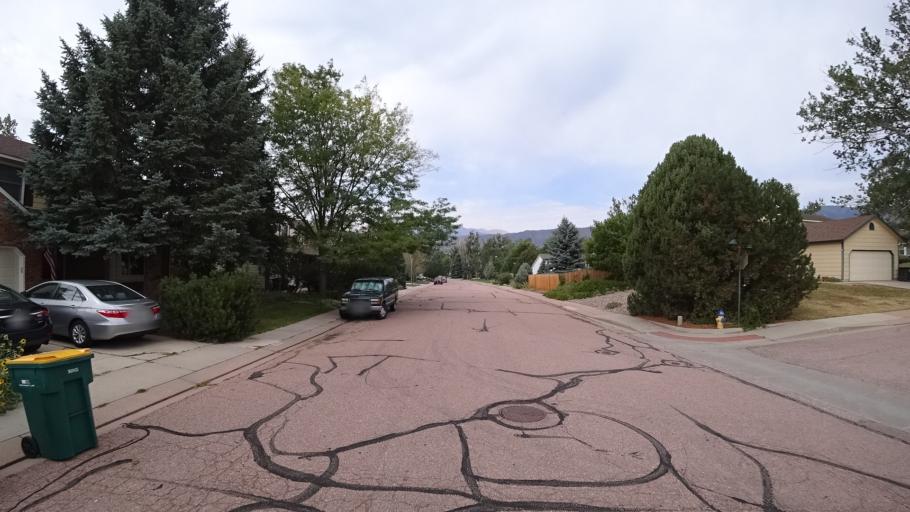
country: US
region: Colorado
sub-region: El Paso County
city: Air Force Academy
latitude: 38.9249
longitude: -104.8378
